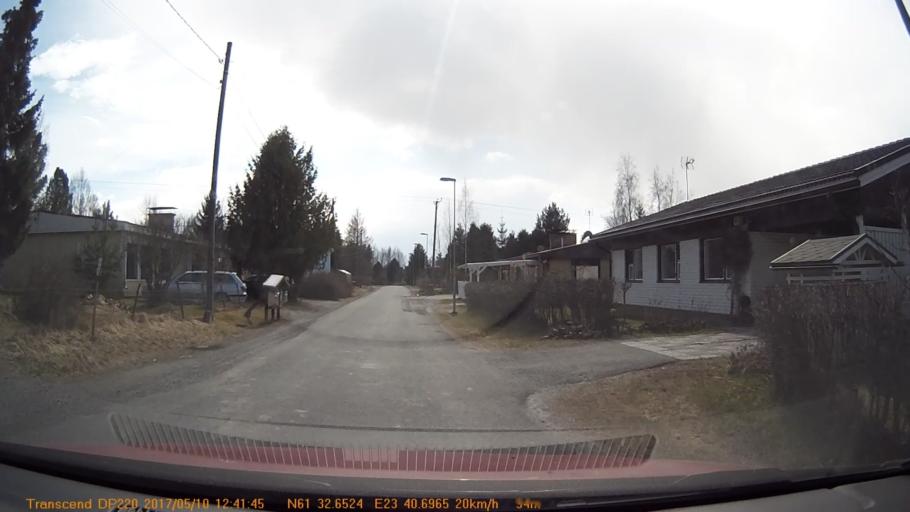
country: FI
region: Pirkanmaa
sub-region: Tampere
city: Yloejaervi
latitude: 61.5441
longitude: 23.6782
